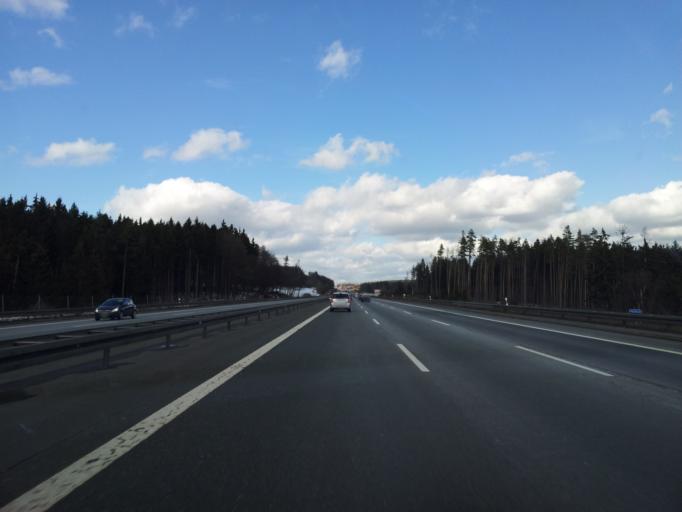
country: DE
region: Bavaria
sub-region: Upper Franconia
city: Leupoldsgrun
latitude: 50.2663
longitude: 11.8021
